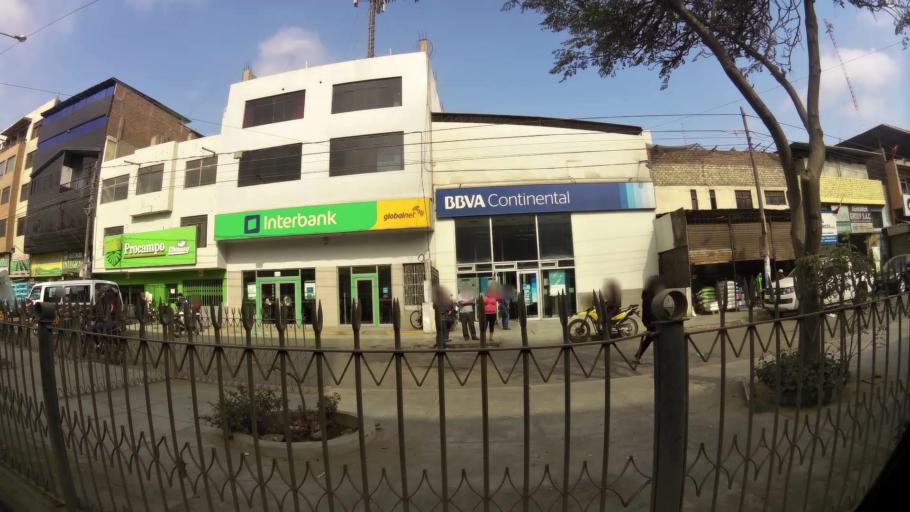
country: PE
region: La Libertad
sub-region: Provincia de Trujillo
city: Trujillo
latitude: -8.1111
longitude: -79.0183
